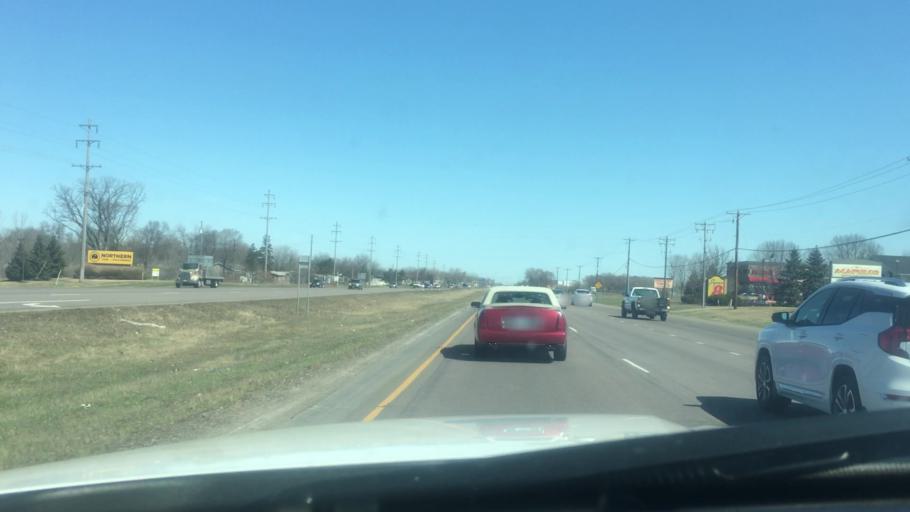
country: US
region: Minnesota
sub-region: Anoka County
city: Blaine
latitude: 45.1408
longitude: -93.2351
